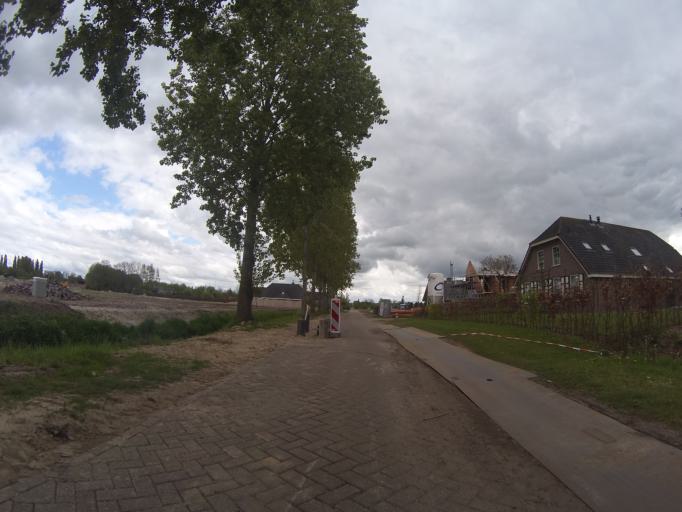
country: NL
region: Gelderland
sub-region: Gemeente Nijkerk
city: Nijkerk
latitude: 52.2246
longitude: 5.4657
